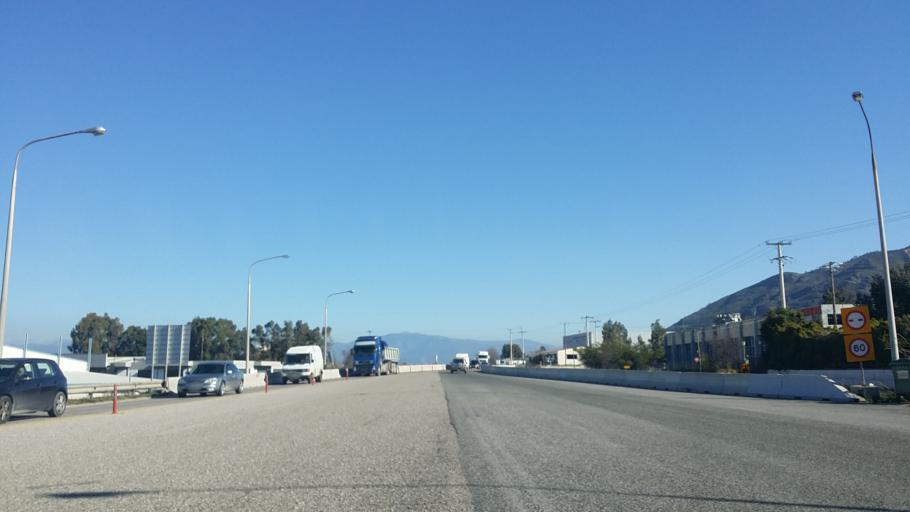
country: GR
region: West Greece
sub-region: Nomos Achaias
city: Rio
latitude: 38.3041
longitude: 21.8032
